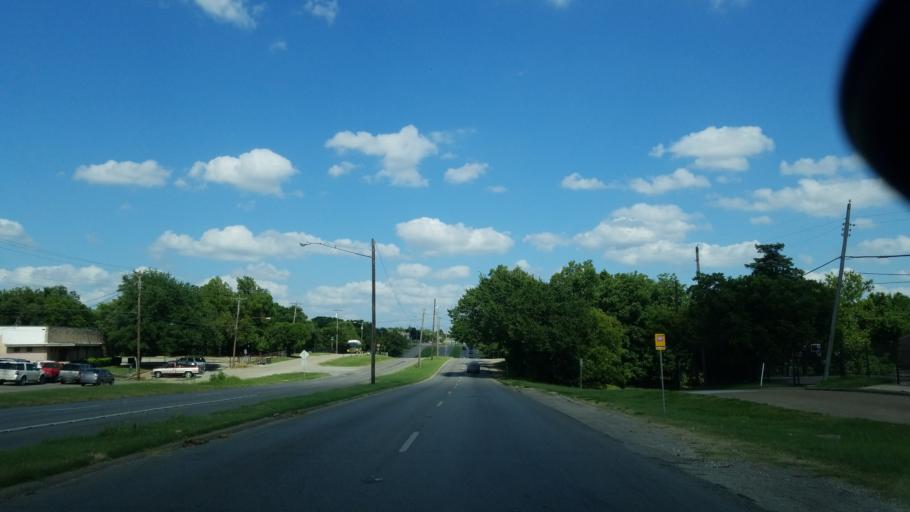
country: US
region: Texas
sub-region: Dallas County
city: Balch Springs
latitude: 32.7720
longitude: -96.6965
